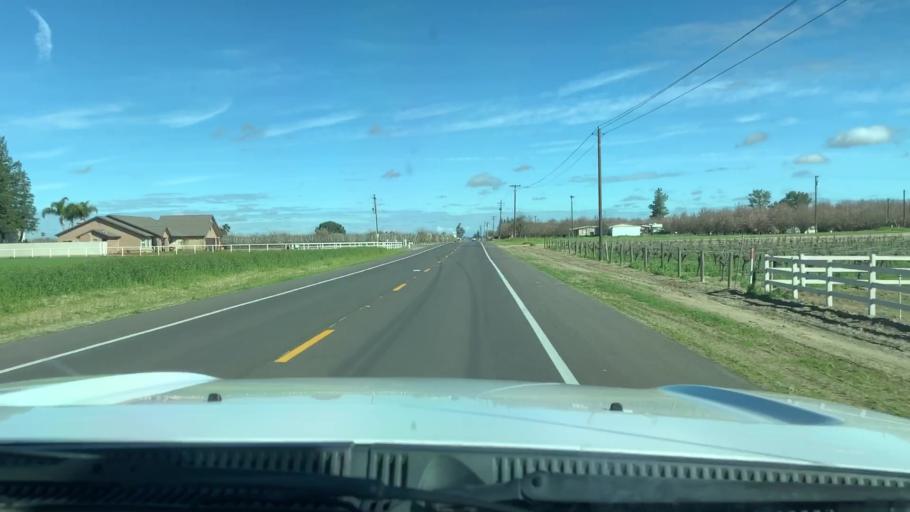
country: US
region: California
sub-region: Fresno County
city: Laton
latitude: 36.4971
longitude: -119.6830
